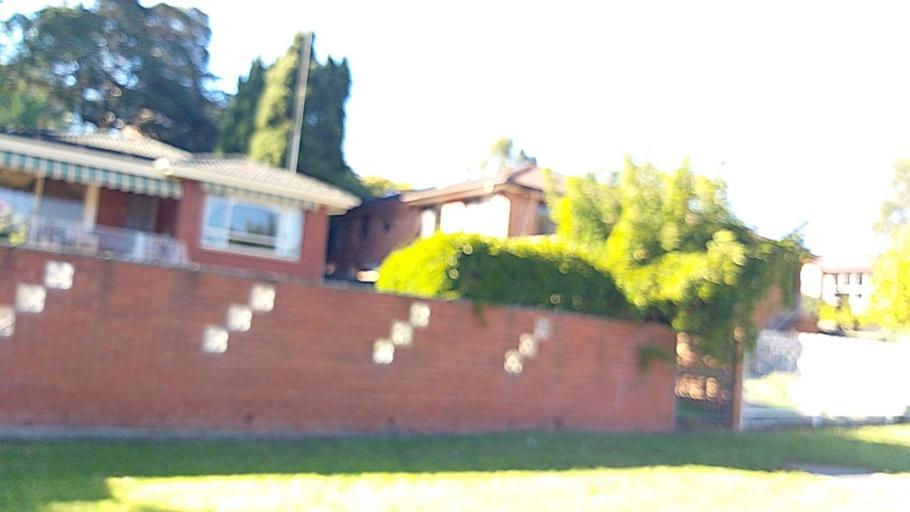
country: AU
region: New South Wales
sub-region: Hunters Hill
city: Gladesville
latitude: -33.8294
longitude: 151.1141
